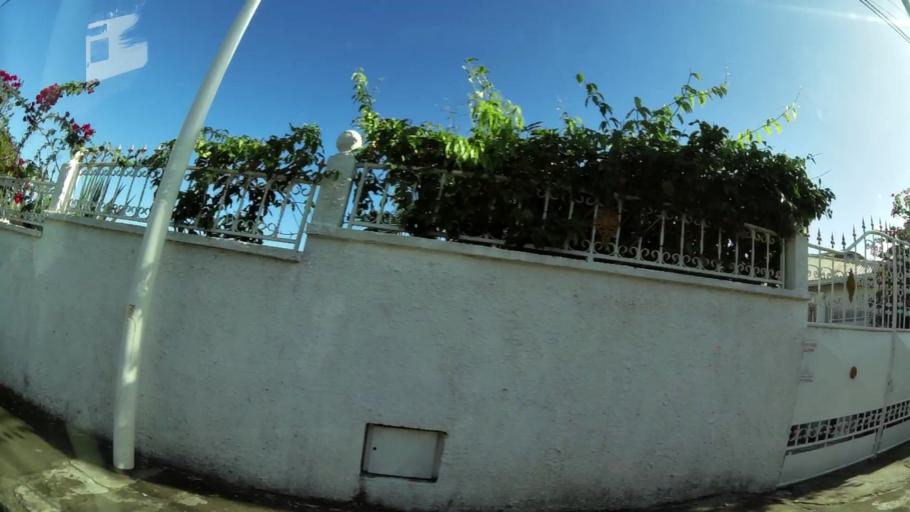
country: GP
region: Guadeloupe
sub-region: Guadeloupe
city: Le Gosier
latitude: 16.2034
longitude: -61.4753
